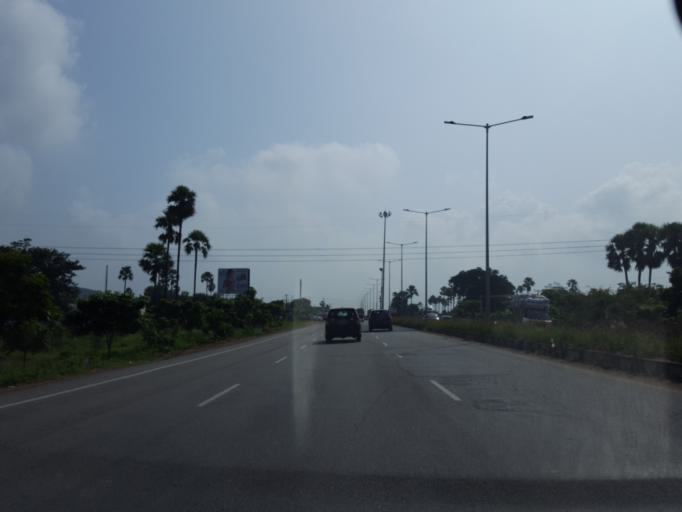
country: IN
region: Telangana
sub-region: Rangareddi
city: Ghatkesar
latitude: 17.3068
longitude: 78.7141
